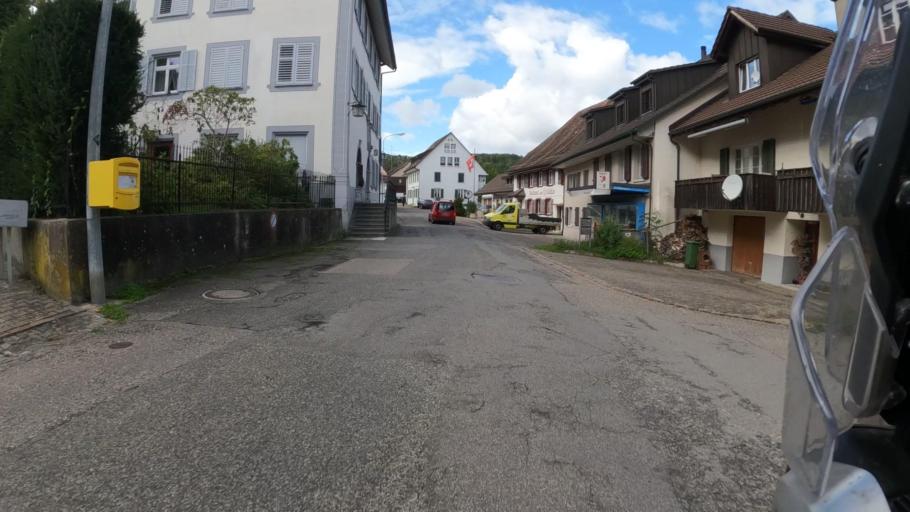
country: CH
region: Aargau
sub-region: Bezirk Zurzach
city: Bad Zurzach
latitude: 47.5701
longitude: 8.3244
